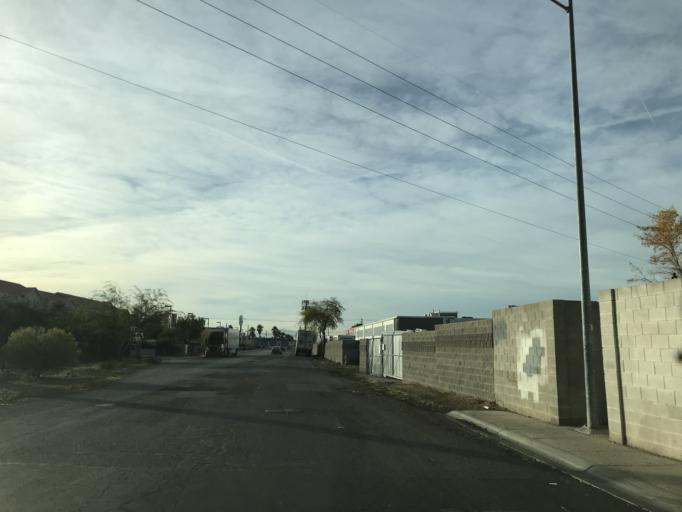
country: US
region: Nevada
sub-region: Clark County
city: Nellis Air Force Base
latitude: 36.2428
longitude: -115.0577
